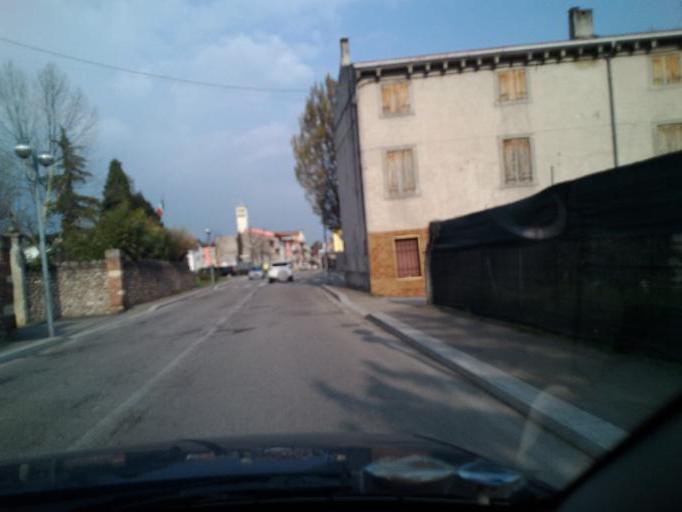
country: IT
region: Veneto
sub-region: Provincia di Verona
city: Caselle
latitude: 45.4152
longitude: 10.8959
